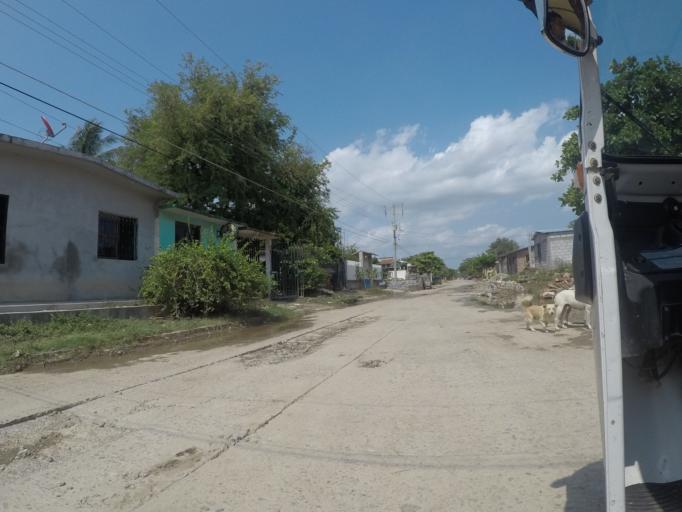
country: MX
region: Oaxaca
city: Union Hidalgo
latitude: 16.4702
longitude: -94.8338
